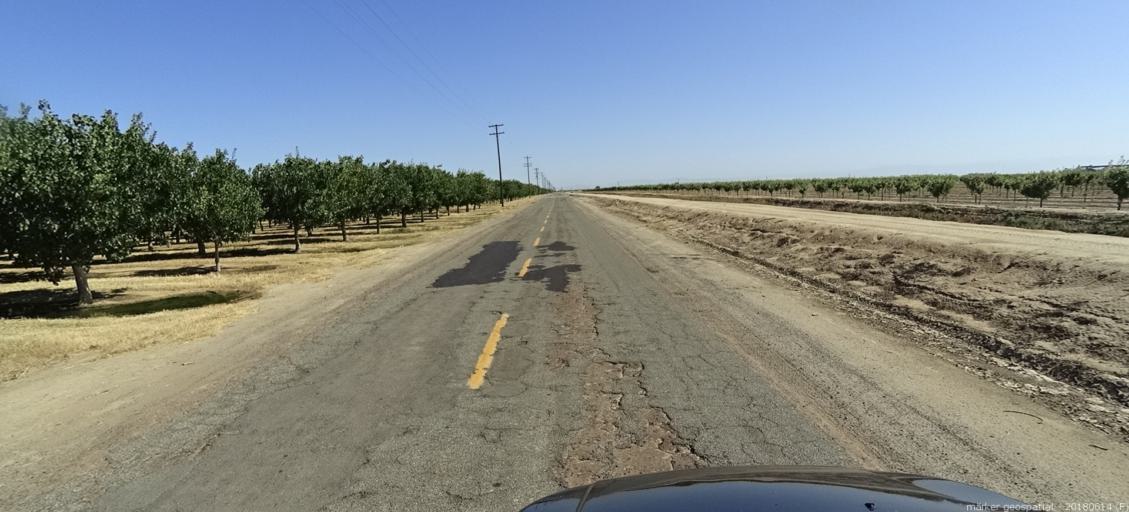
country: US
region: California
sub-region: Madera County
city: Fairmead
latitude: 37.0342
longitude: -120.1660
